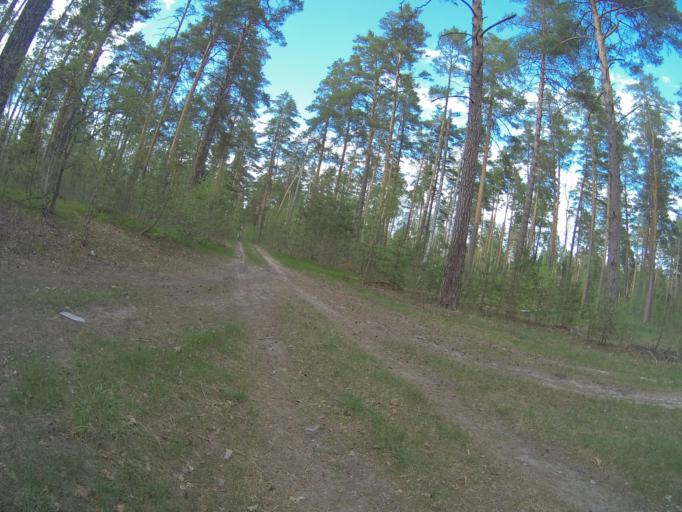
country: RU
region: Vladimir
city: Orgtrud
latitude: 56.1207
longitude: 40.7235
